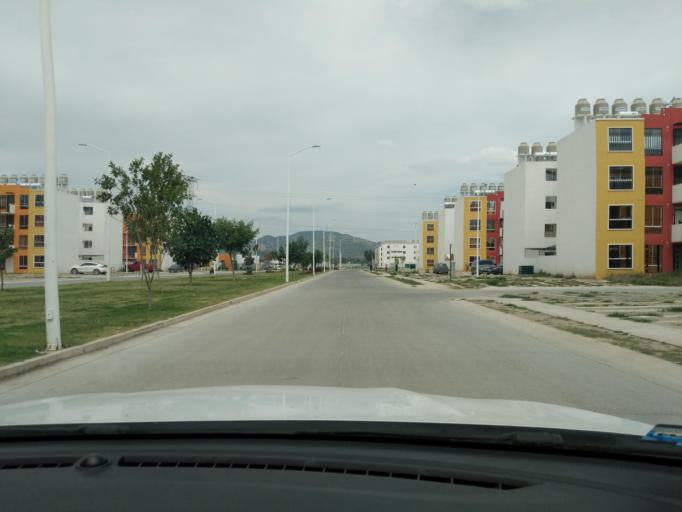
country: MX
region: Jalisco
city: Tesistan
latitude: 20.7835
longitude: -103.4877
